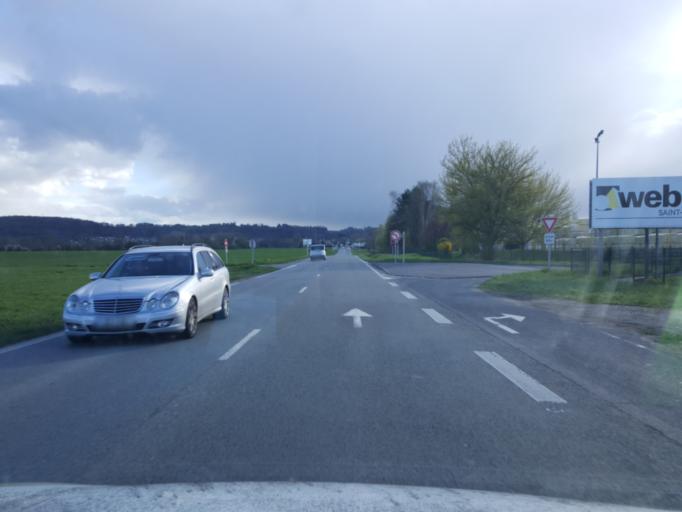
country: FR
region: Picardie
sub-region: Departement de l'Oise
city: Auneuil
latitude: 49.3903
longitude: 2.0080
